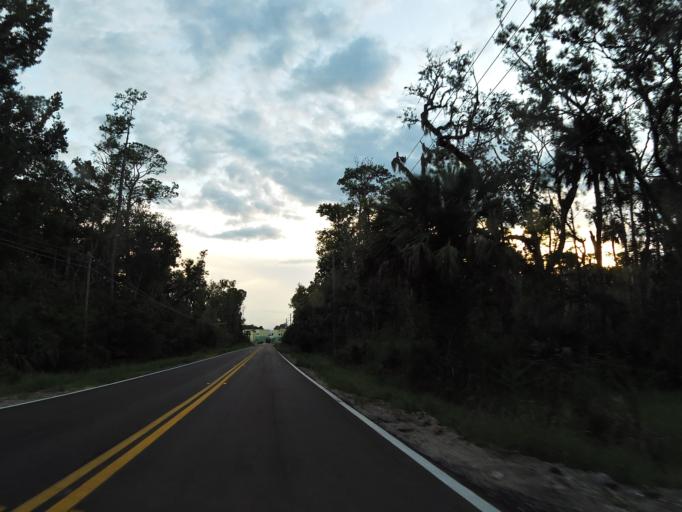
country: US
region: Florida
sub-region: Saint Johns County
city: Palm Valley
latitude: 30.1234
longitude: -81.4038
